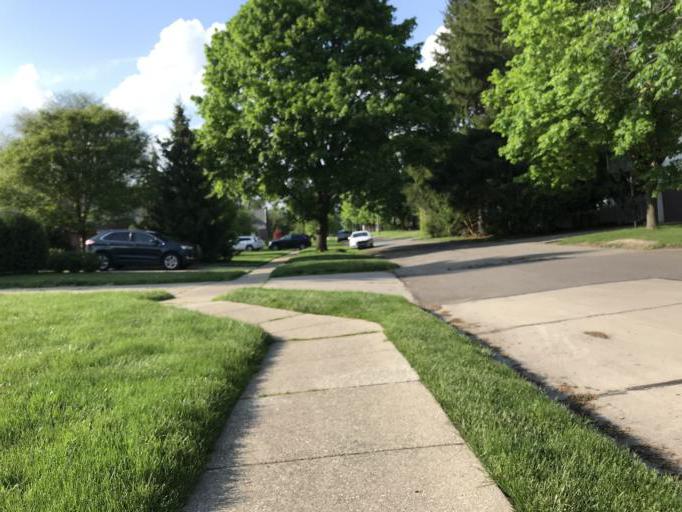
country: US
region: Michigan
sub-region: Oakland County
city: Farmington
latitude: 42.4638
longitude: -83.3828
